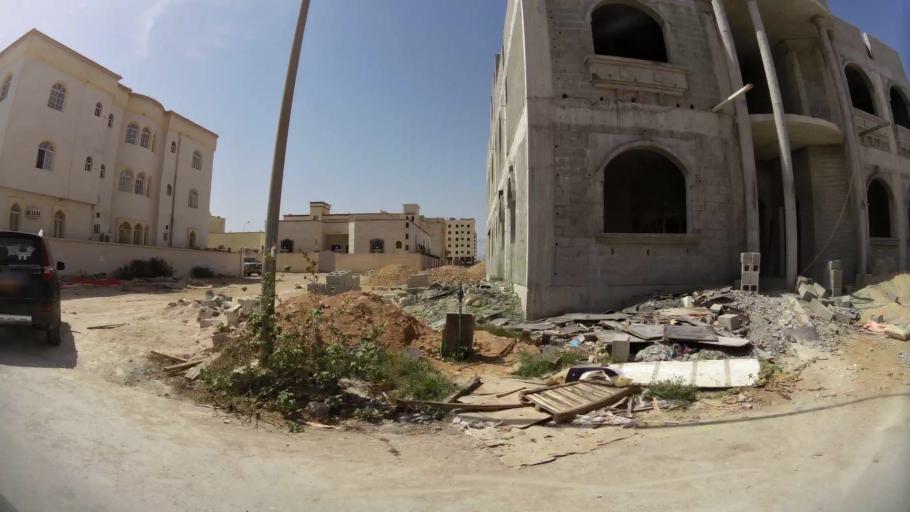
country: OM
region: Zufar
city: Salalah
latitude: 17.0487
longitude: 54.1600
